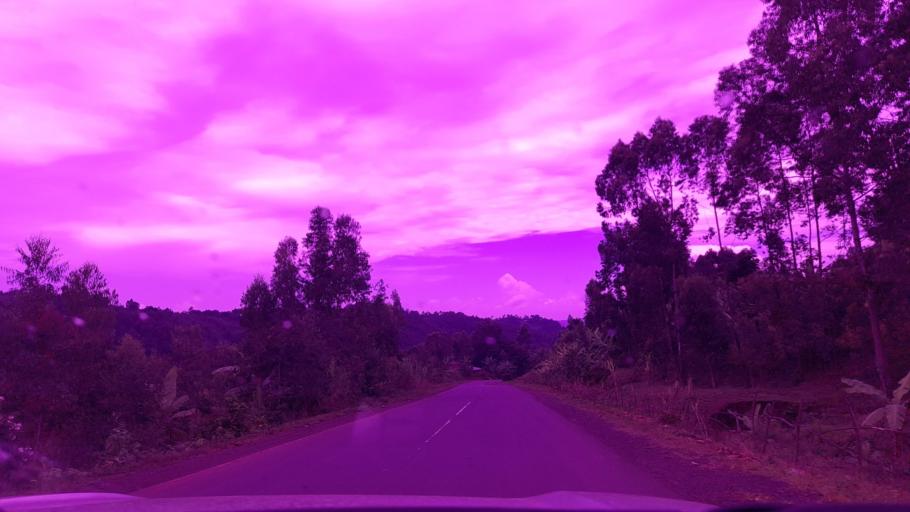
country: ET
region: Southern Nations, Nationalities, and People's Region
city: Mizan Teferi
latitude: 7.0646
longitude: 35.6316
